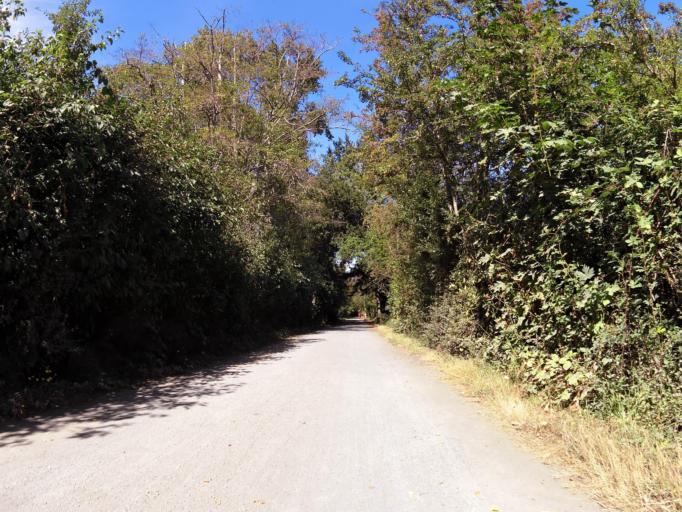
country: CA
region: British Columbia
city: Victoria
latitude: 48.5417
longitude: -123.3823
